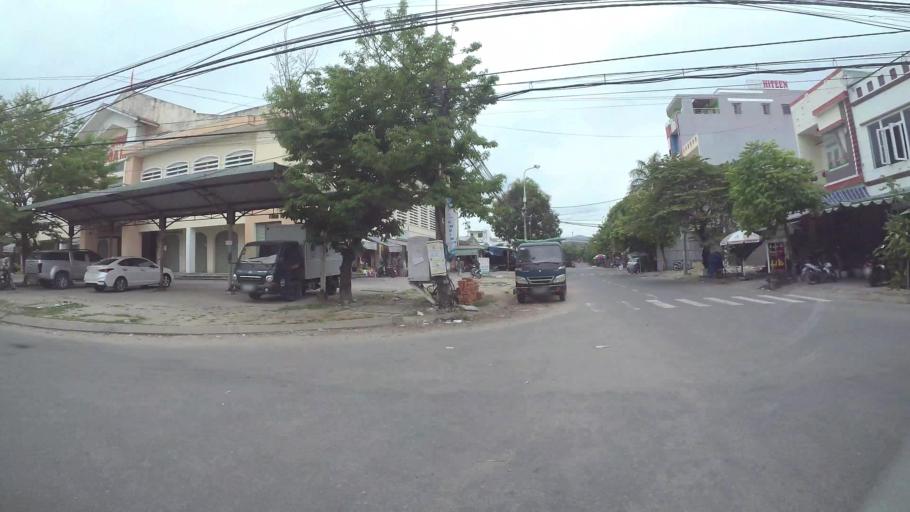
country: VN
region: Da Nang
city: Lien Chieu
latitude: 16.0593
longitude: 108.1705
